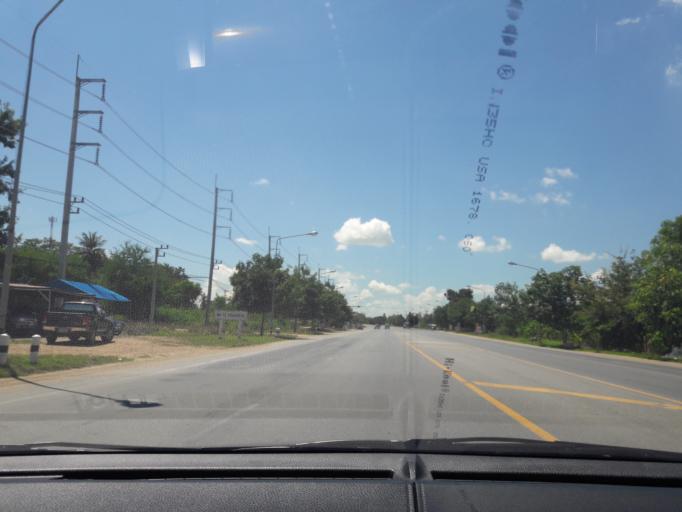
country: TH
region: Kanchanaburi
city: Tha Maka
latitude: 14.0344
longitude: 99.8193
